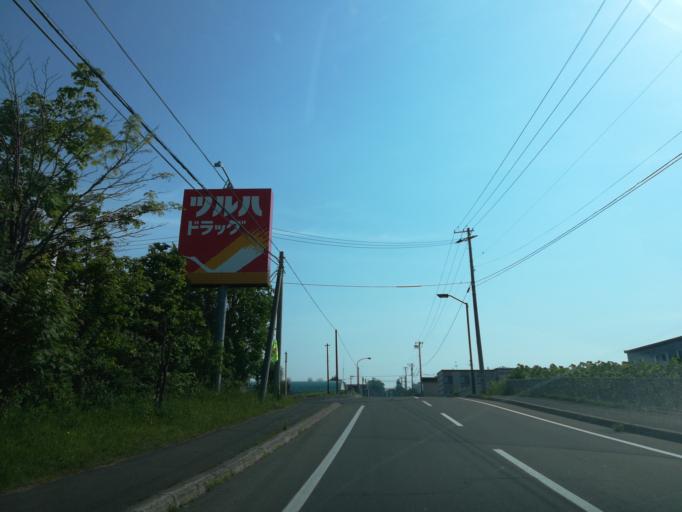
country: JP
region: Hokkaido
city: Iwamizawa
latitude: 43.2116
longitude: 141.7783
